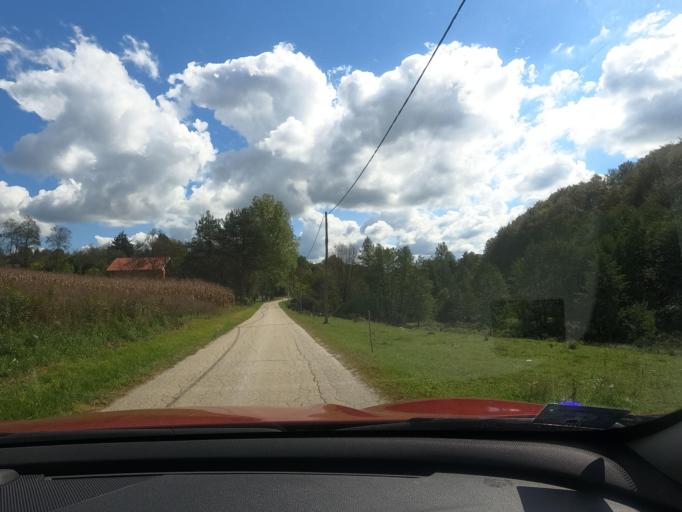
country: BA
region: Federation of Bosnia and Herzegovina
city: Velika Kladusa
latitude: 45.2329
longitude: 15.7673
